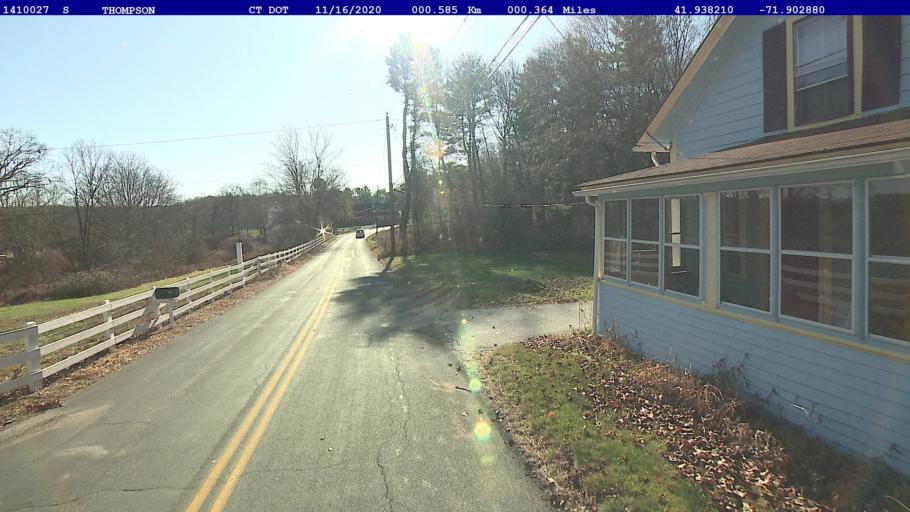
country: US
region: Connecticut
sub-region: Windham County
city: Putnam
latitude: 41.9382
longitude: -71.9029
